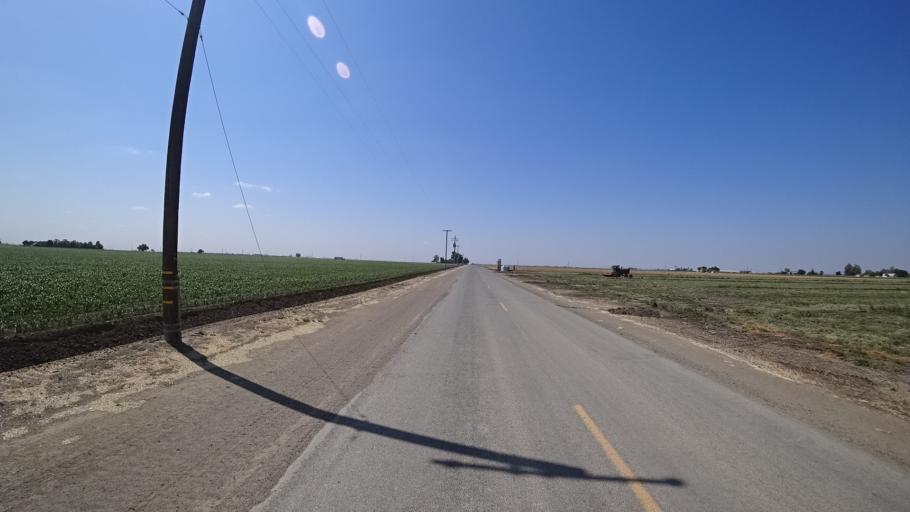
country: US
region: California
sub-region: Kings County
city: Home Garden
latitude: 36.2162
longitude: -119.6279
